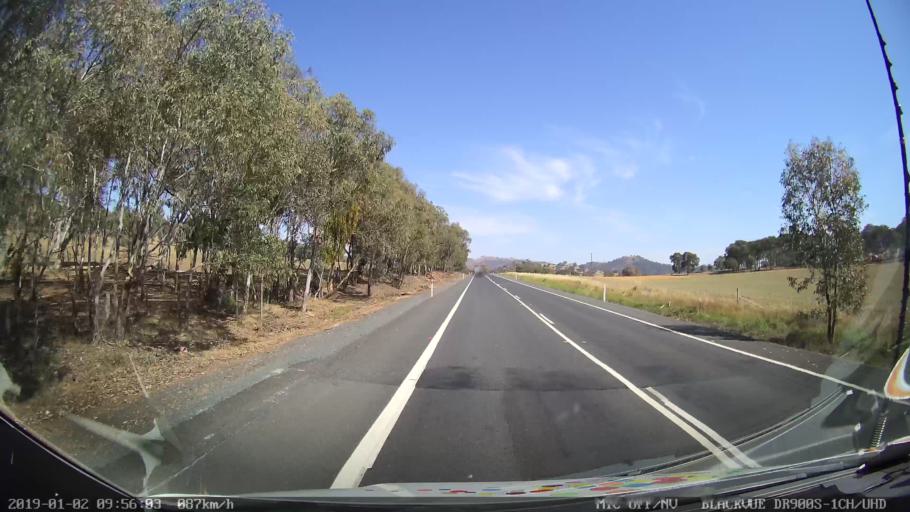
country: AU
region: New South Wales
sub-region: Tumut Shire
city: Tumut
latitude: -35.2187
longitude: 148.1805
